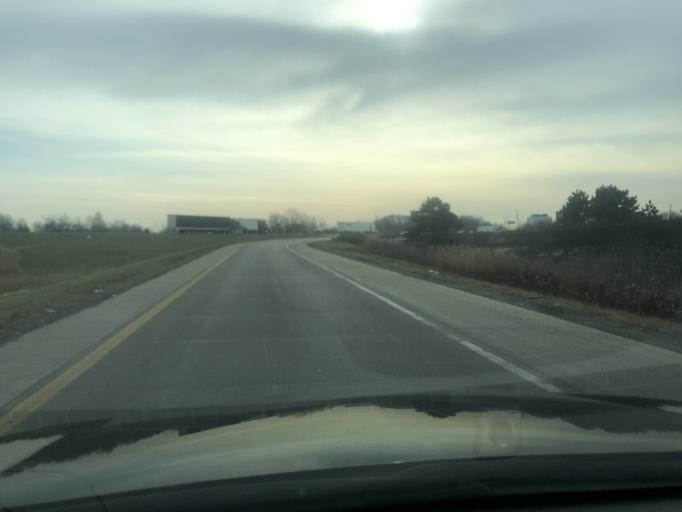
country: US
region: Michigan
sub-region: Wayne County
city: Southgate
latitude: 42.2086
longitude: -83.2304
